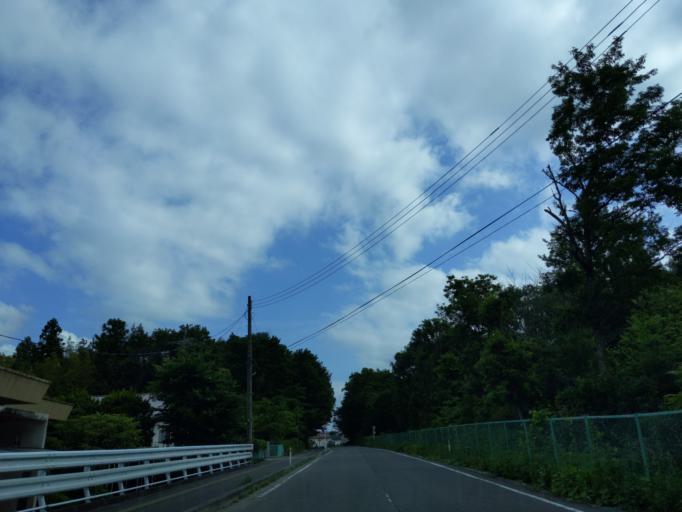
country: JP
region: Fukushima
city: Sukagawa
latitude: 37.2921
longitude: 140.3899
